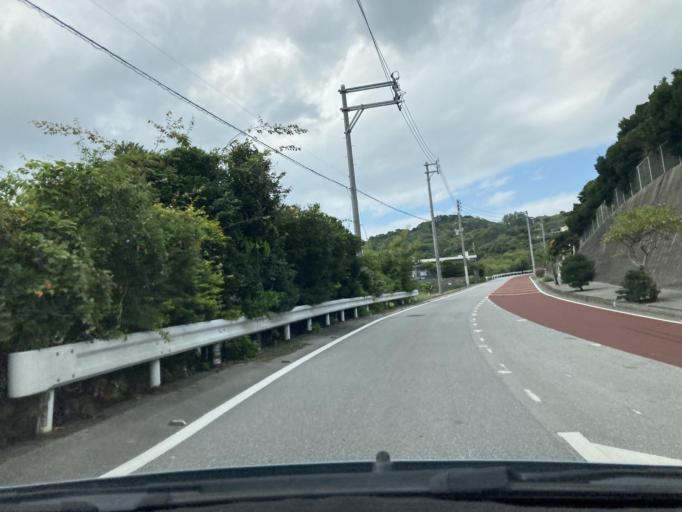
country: JP
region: Okinawa
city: Ginowan
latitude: 26.2557
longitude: 127.7842
